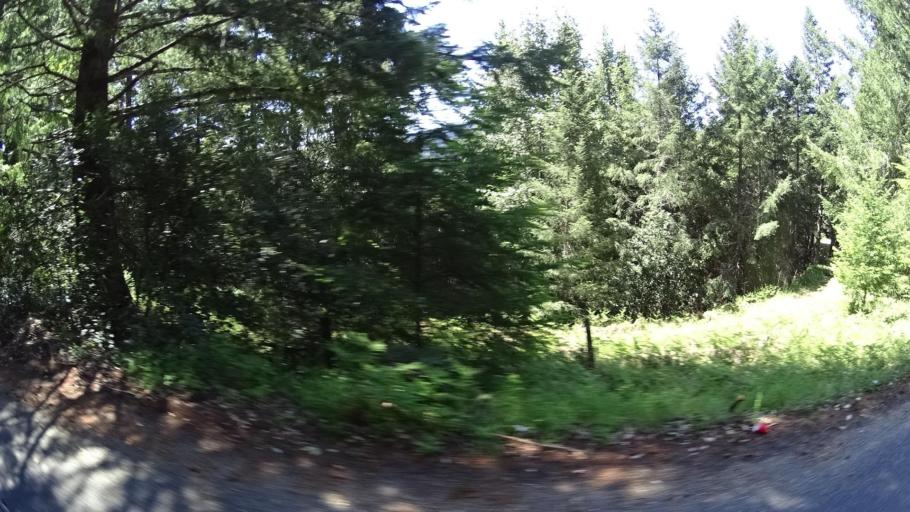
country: US
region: California
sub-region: Humboldt County
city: Redway
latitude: 40.1508
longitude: -124.0328
